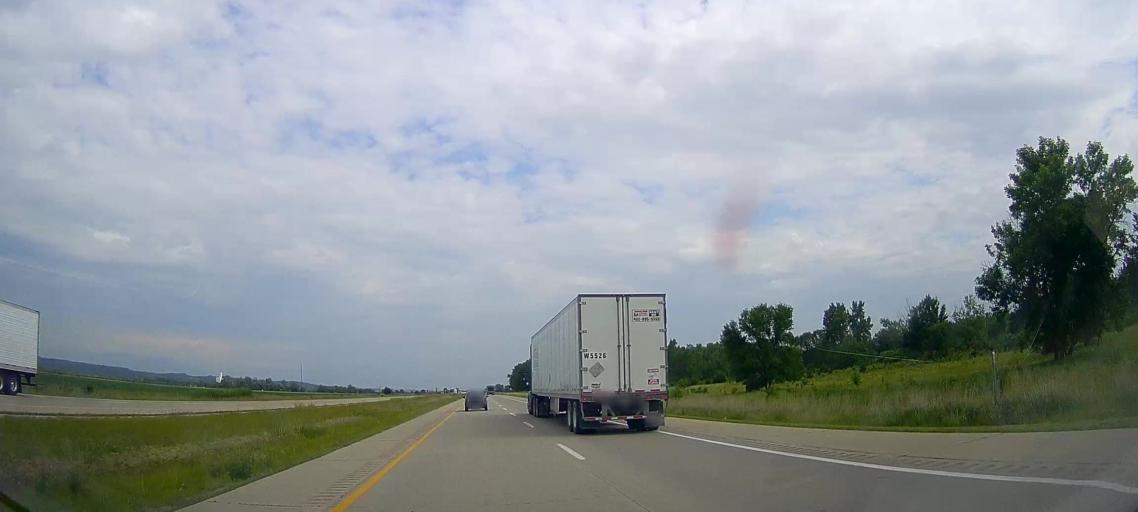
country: US
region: Nebraska
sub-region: Burt County
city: Tekamah
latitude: 41.8135
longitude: -96.0662
